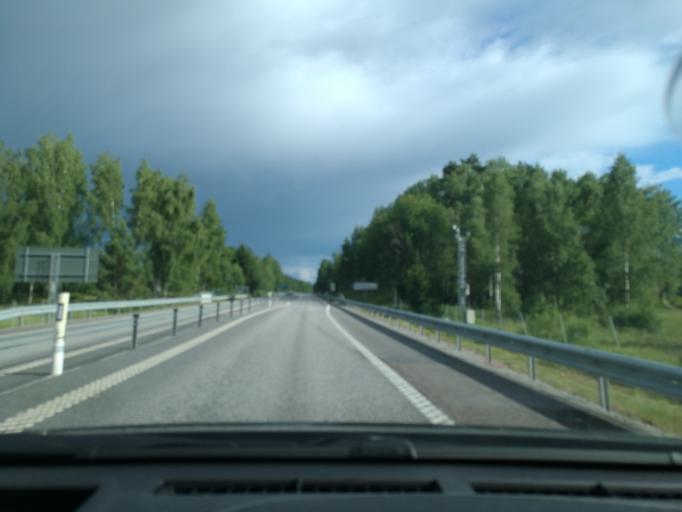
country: SE
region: Vaestmanland
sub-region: Surahammars Kommun
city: Surahammar
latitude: 59.7196
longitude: 16.2385
